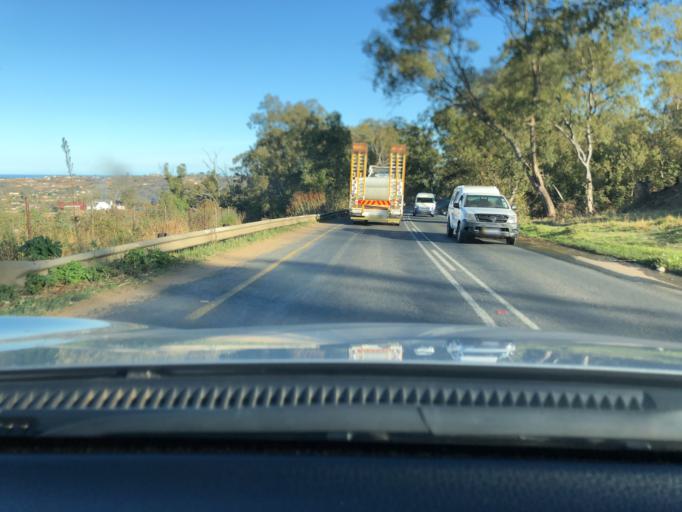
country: ZA
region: KwaZulu-Natal
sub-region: eThekwini Metropolitan Municipality
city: Umkomaas
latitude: -30.0261
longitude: 30.8122
